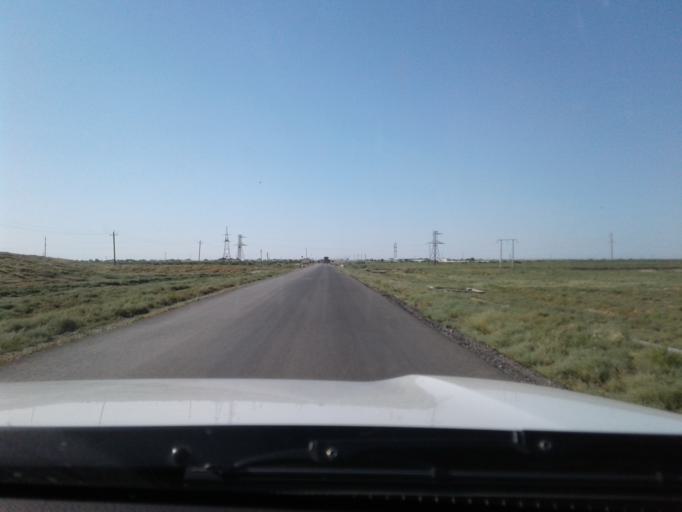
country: IR
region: Razavi Khorasan
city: Kalat-e Naderi
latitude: 37.1817
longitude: 60.0418
